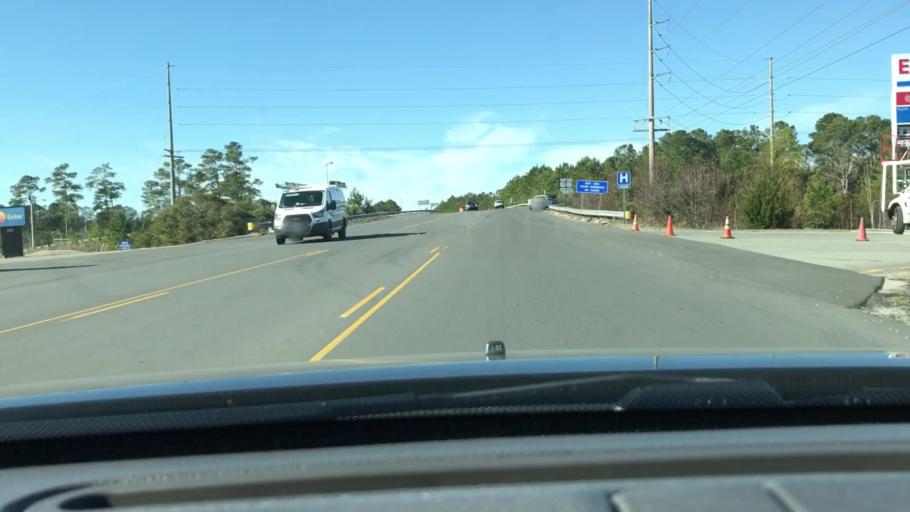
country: US
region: North Carolina
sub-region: Brunswick County
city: Shallotte
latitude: 33.9747
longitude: -78.4020
